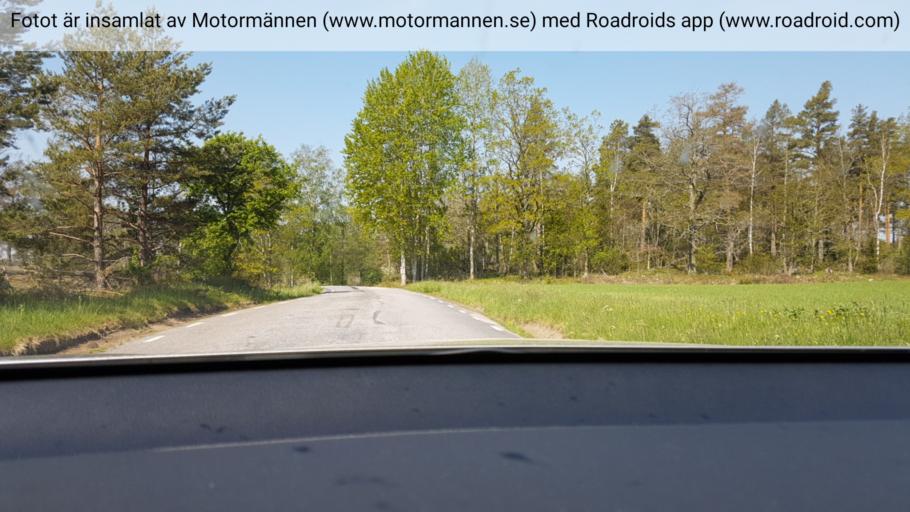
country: SE
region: Kalmar
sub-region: Vasterviks Kommun
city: Gamleby
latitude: 57.8710
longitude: 16.4603
